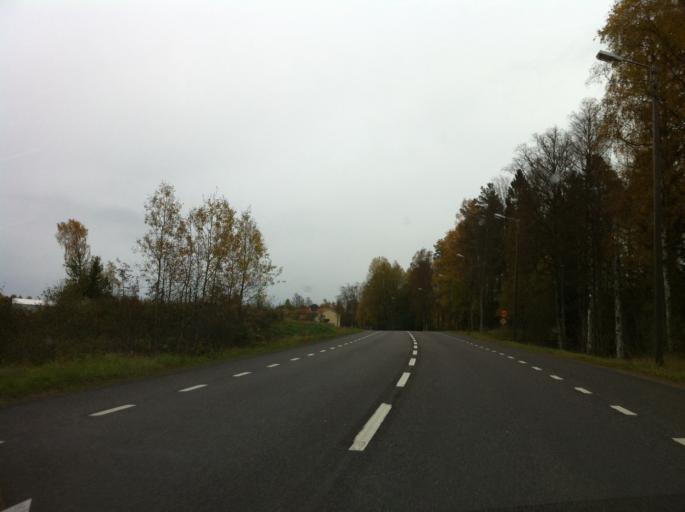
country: SE
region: Dalarna
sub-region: Ludvika Kommun
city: Grangesberg
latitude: 60.0714
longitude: 14.9946
